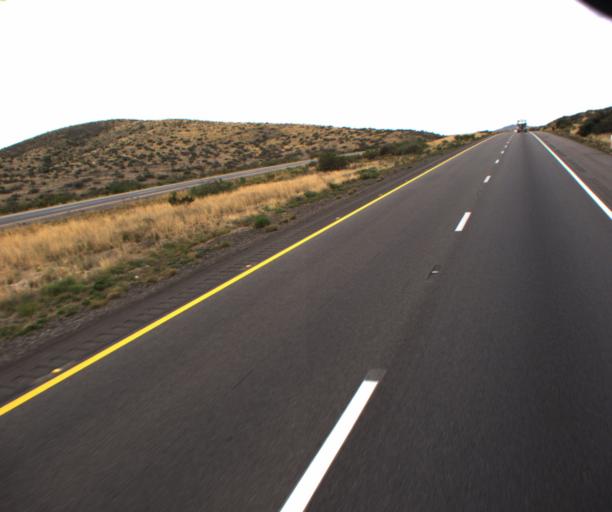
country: US
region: Arizona
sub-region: Cochise County
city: Willcox
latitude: 32.1165
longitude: -110.0199
